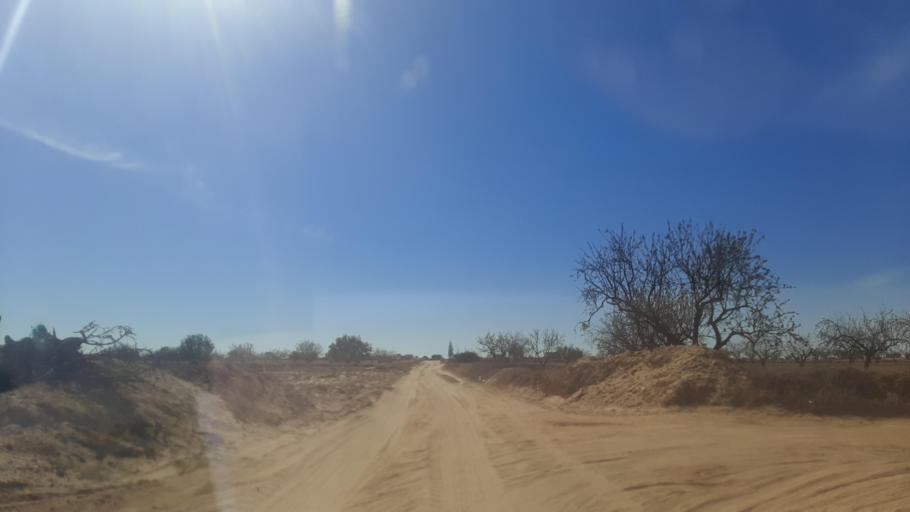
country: TN
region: Safaqis
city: Sfax
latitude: 34.8521
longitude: 10.5625
